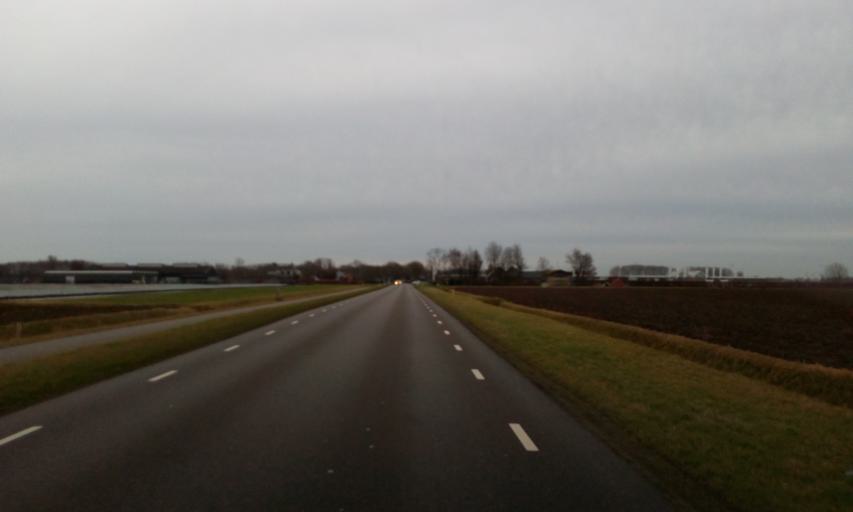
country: NL
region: North Brabant
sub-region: Gemeente Woudrichem
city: Woudrichem
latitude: 51.8036
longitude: 5.0043
